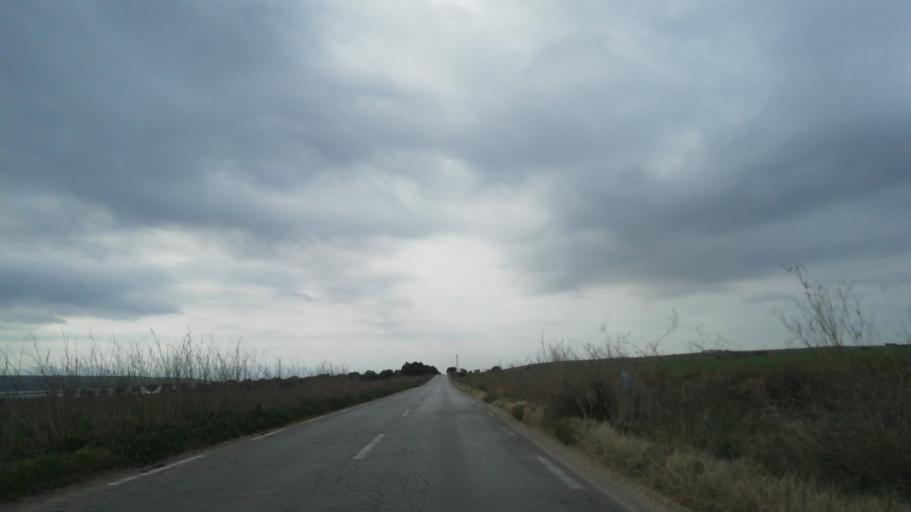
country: DZ
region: Oran
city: Sidi ech Chahmi
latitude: 35.6188
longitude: -0.4150
